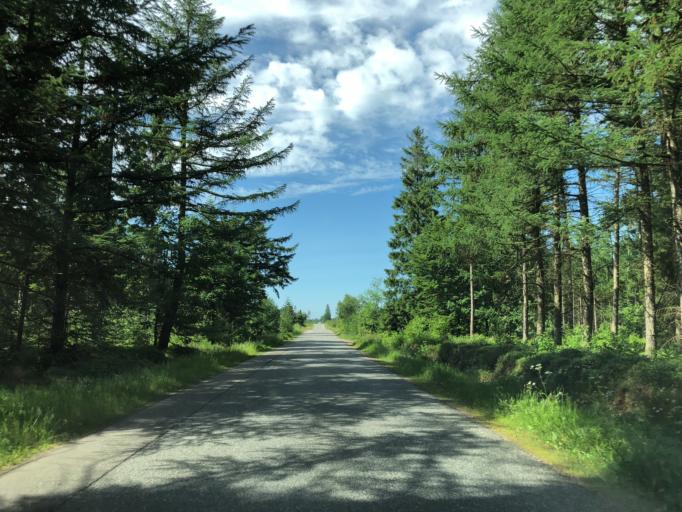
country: DK
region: Central Jutland
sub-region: Herning Kommune
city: Lind
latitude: 56.0457
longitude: 8.9314
